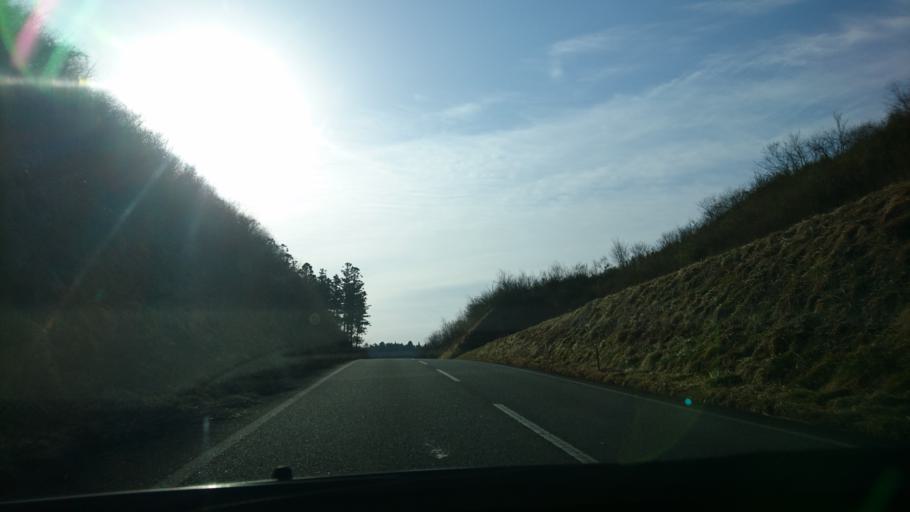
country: JP
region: Iwate
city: Ichinoseki
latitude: 38.8636
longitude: 141.1946
